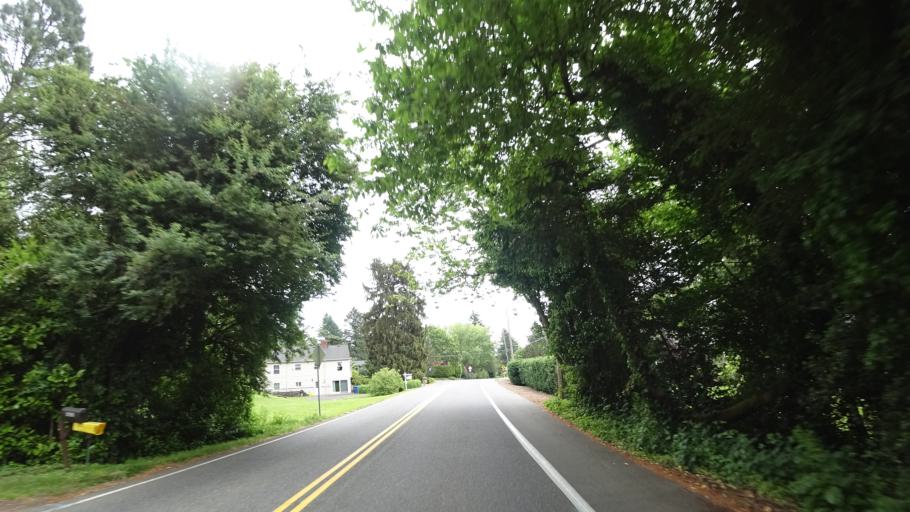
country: US
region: Oregon
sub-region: Multnomah County
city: Portland
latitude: 45.4823
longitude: -122.6972
